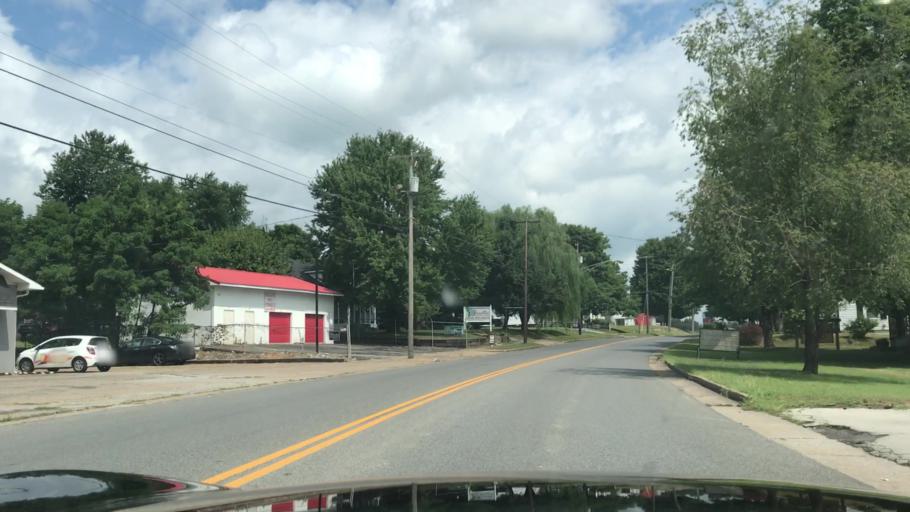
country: US
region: Kentucky
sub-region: Muhlenberg County
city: Greenville
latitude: 37.2097
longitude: -87.1806
